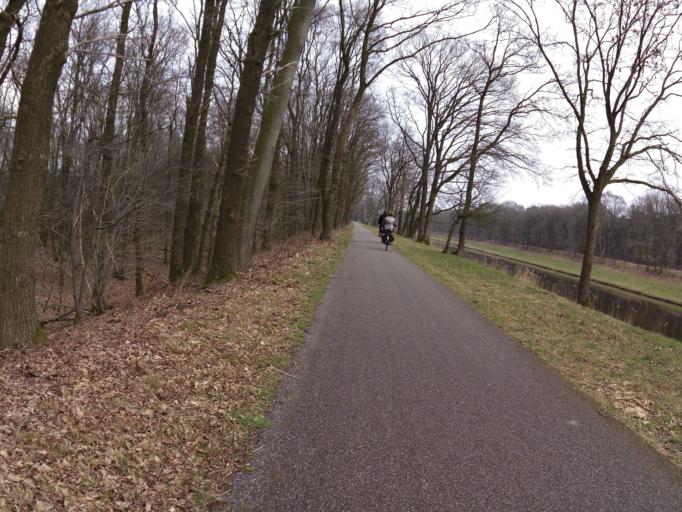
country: NL
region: North Brabant
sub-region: Gemeente Heusden
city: Heusden
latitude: 51.6689
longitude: 5.1549
